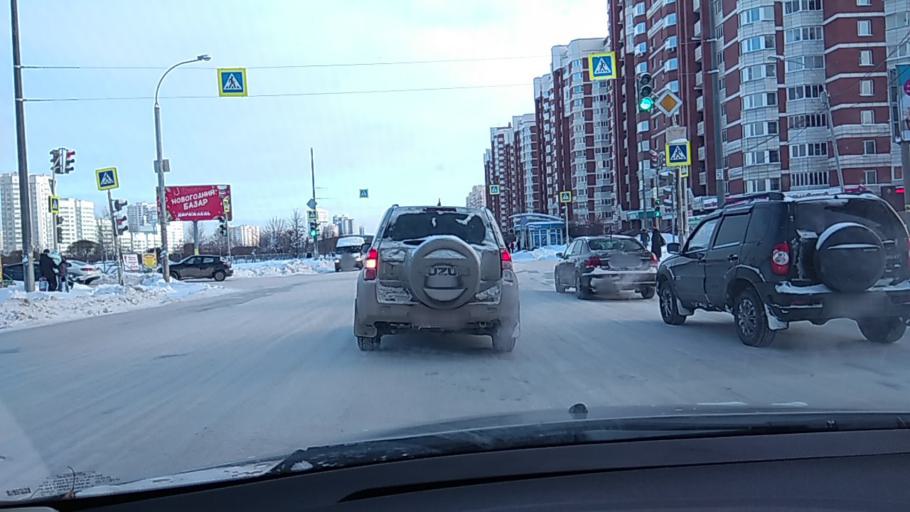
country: RU
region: Sverdlovsk
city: Yekaterinburg
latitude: 56.7959
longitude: 60.6135
